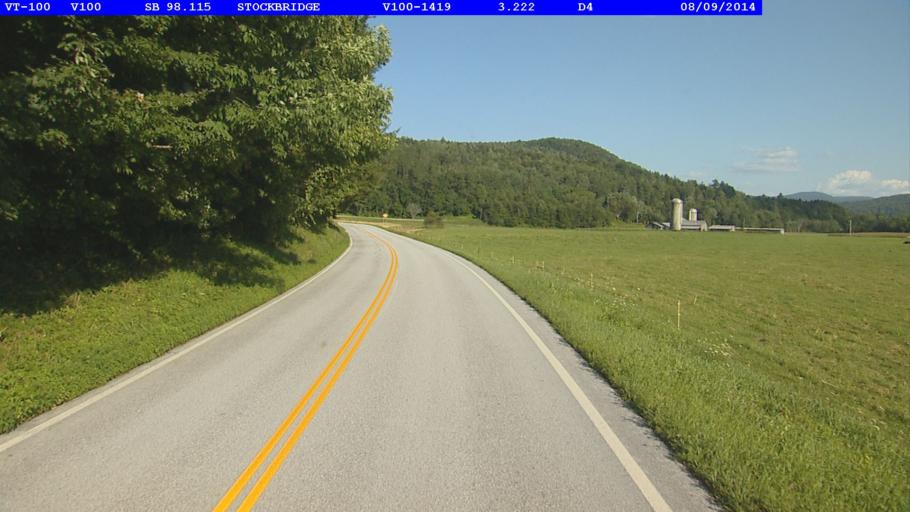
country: US
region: Vermont
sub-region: Orange County
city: Randolph
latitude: 43.7858
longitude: -72.7588
